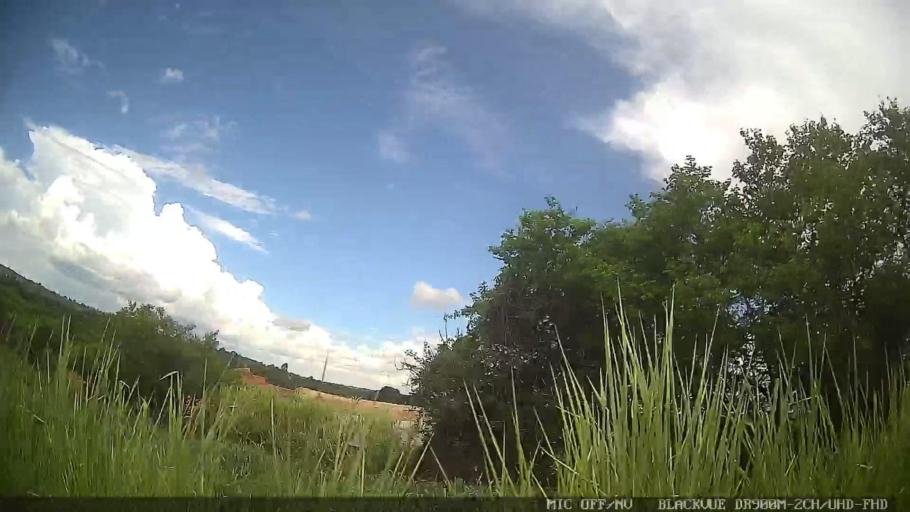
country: BR
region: Sao Paulo
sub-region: Conchas
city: Conchas
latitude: -23.0212
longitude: -47.9979
